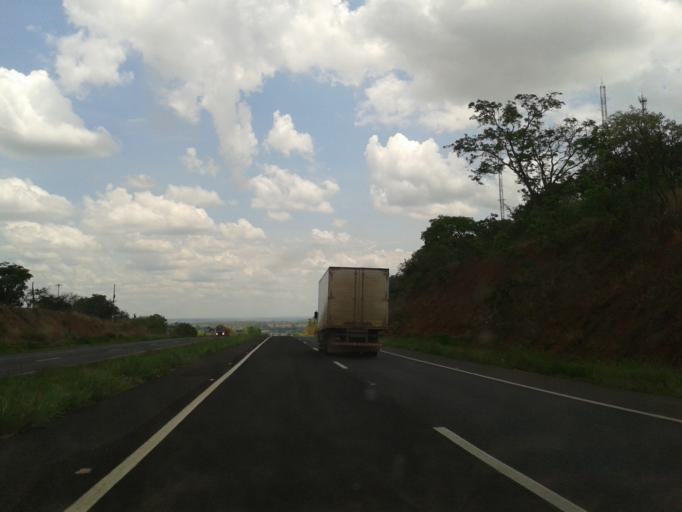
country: BR
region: Minas Gerais
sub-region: Monte Alegre De Minas
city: Monte Alegre de Minas
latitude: -18.8550
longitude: -48.8548
